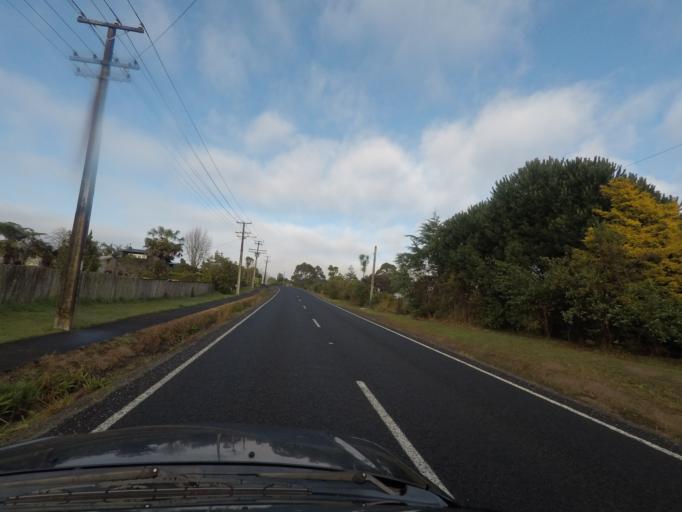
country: NZ
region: Auckland
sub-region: Auckland
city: Waitakere
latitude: -36.9015
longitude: 174.6137
